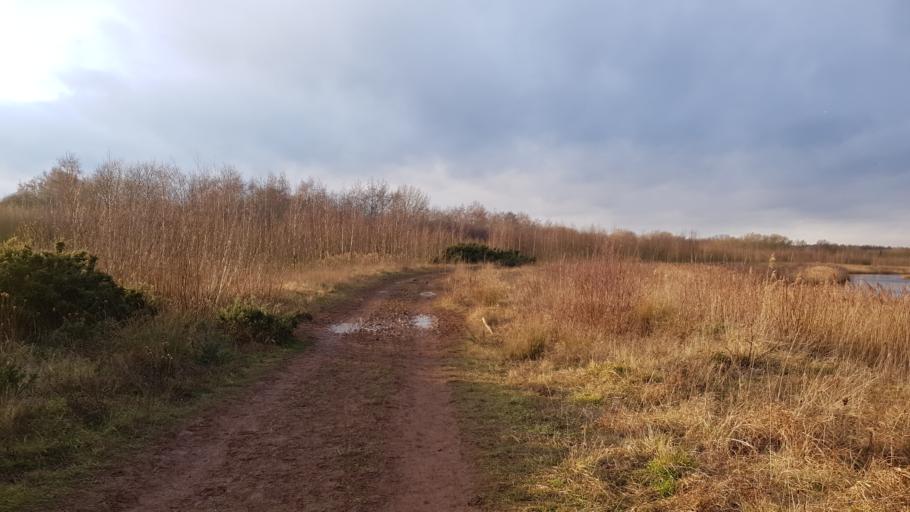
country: GB
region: England
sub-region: City and Borough of Leeds
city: Swillington
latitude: 53.7457
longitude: -1.4155
